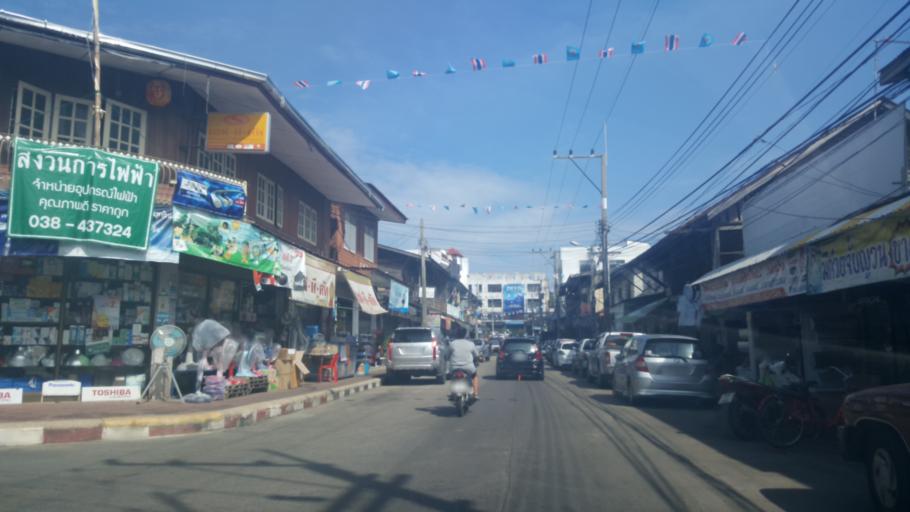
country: TH
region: Chon Buri
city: Sattahip
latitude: 12.6640
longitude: 100.9014
